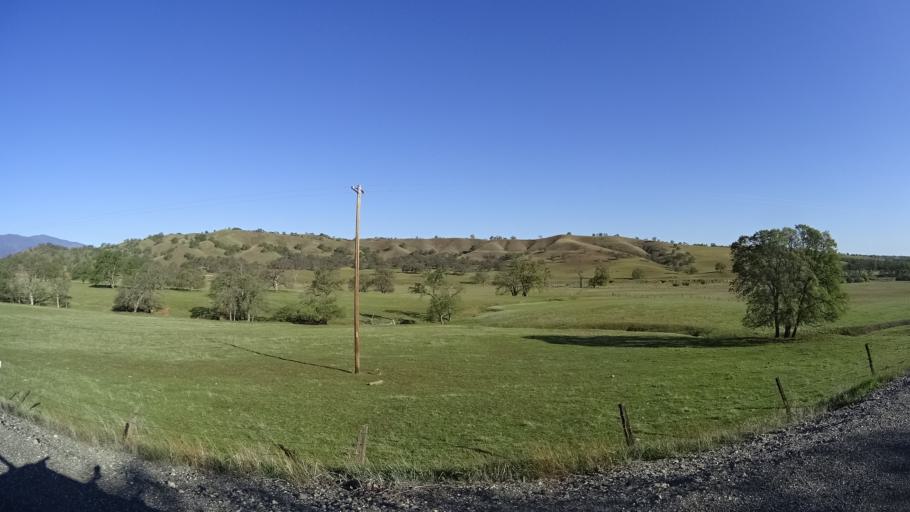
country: US
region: California
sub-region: Tehama County
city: Rancho Tehama Reserve
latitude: 39.7863
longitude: -122.4640
